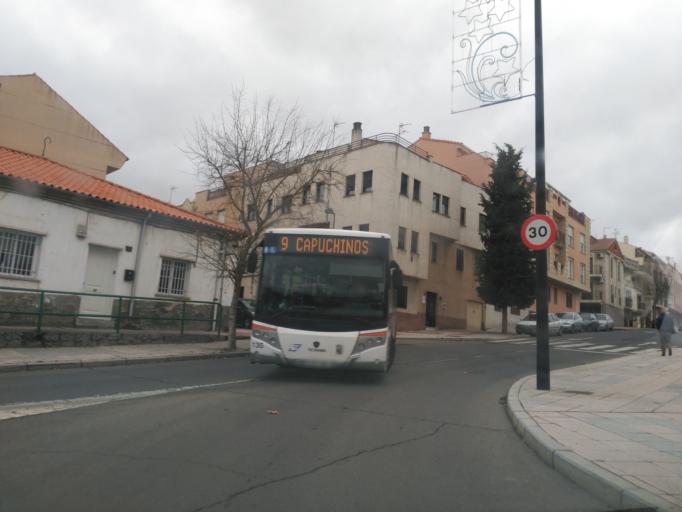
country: ES
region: Castille and Leon
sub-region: Provincia de Salamanca
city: Salamanca
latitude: 40.9523
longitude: -5.6708
